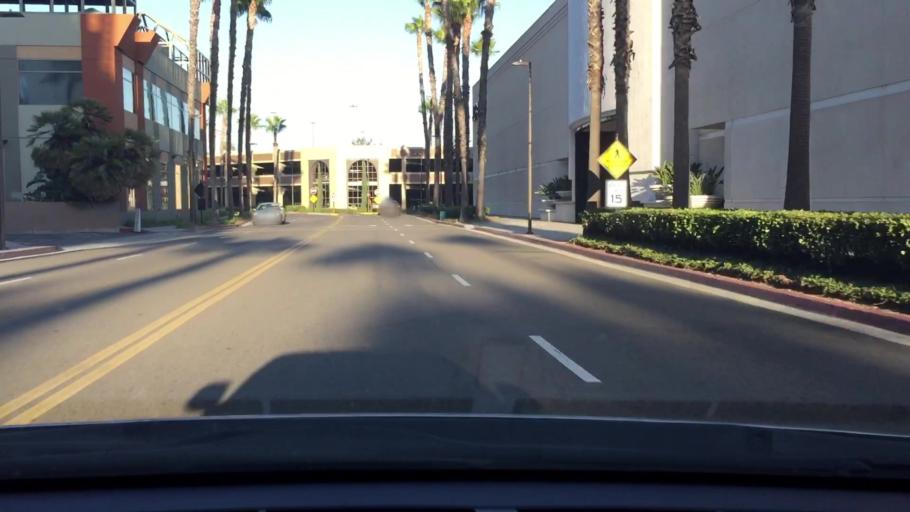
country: US
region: California
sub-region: Orange County
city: Brea
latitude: 33.9157
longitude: -117.8886
